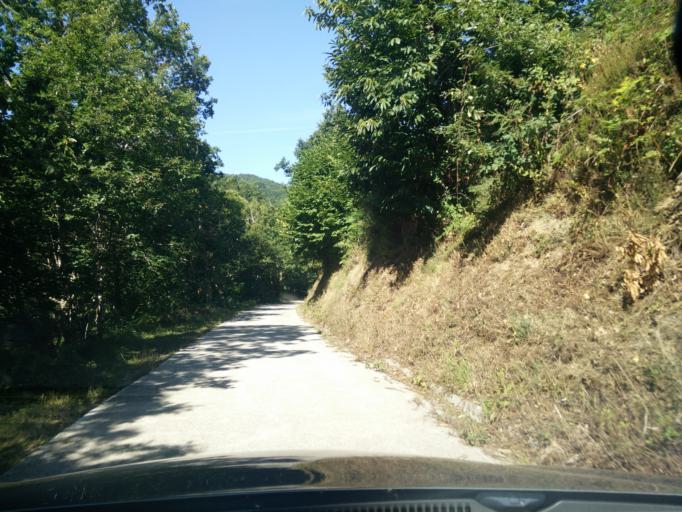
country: ES
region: Asturias
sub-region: Province of Asturias
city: Campo de Caso
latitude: 43.1505
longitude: -5.3811
